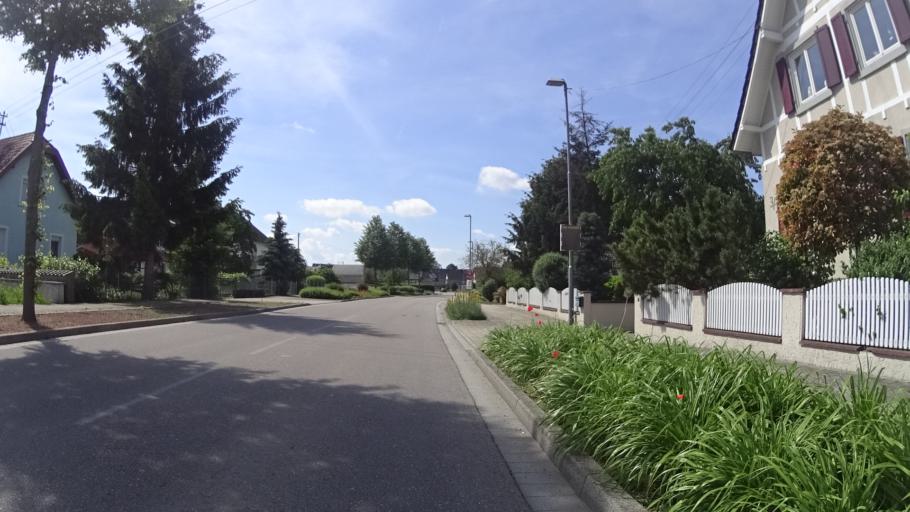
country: DE
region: Baden-Wuerttemberg
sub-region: Freiburg Region
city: Meissenheim
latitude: 48.4705
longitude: 7.8120
